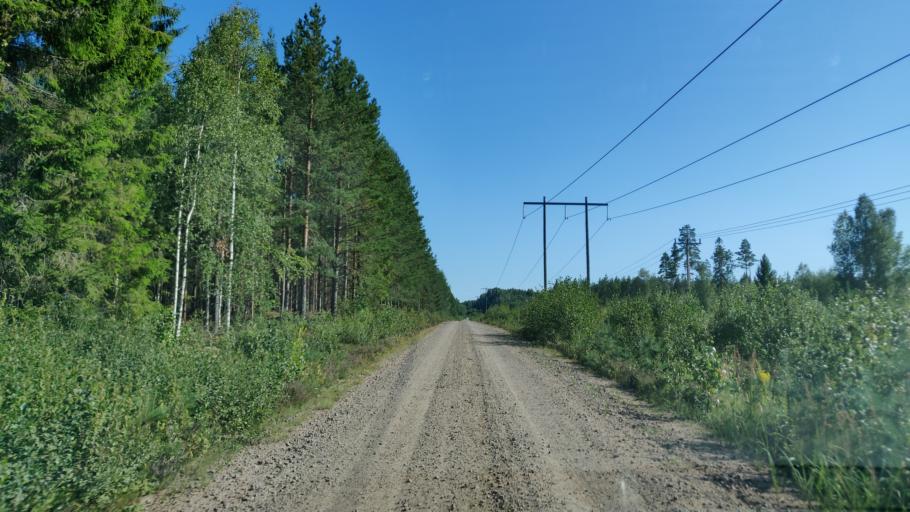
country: SE
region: Vaermland
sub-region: Hagfors Kommun
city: Ekshaerad
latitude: 60.0536
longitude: 13.5221
